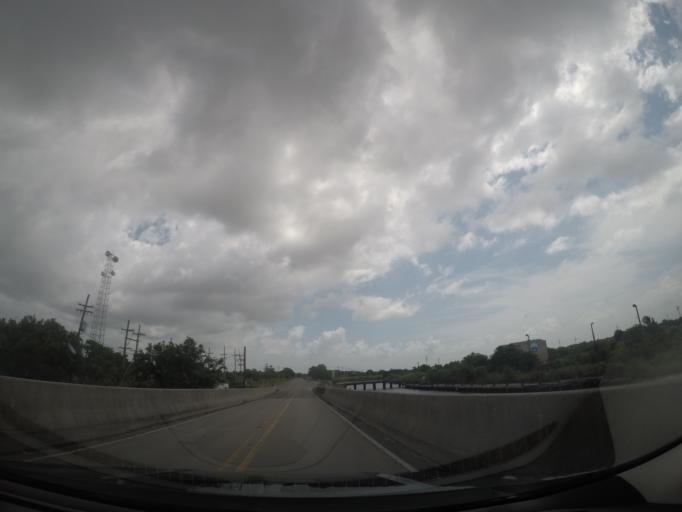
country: US
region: Louisiana
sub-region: Saint Tammany Parish
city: Eden Isle
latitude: 30.0685
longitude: -89.8037
